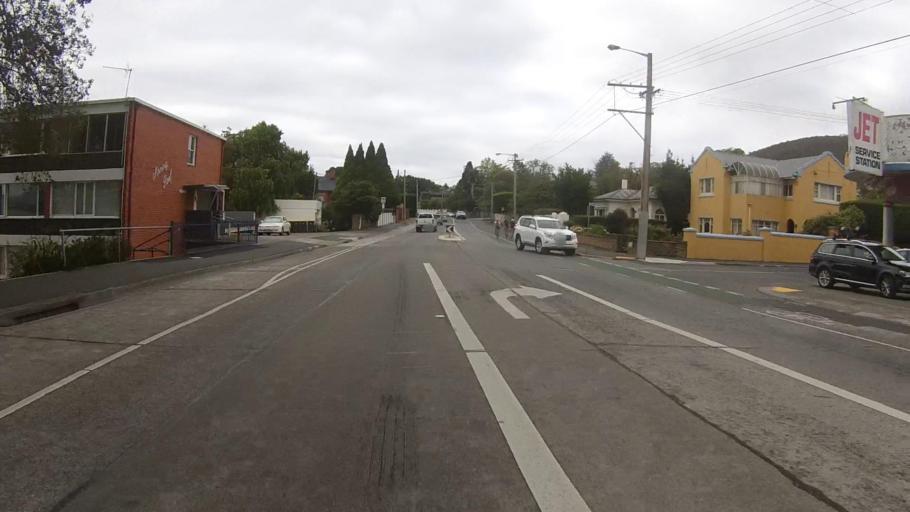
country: AU
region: Tasmania
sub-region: Hobart
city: Sandy Bay
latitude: -42.9069
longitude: 147.3425
